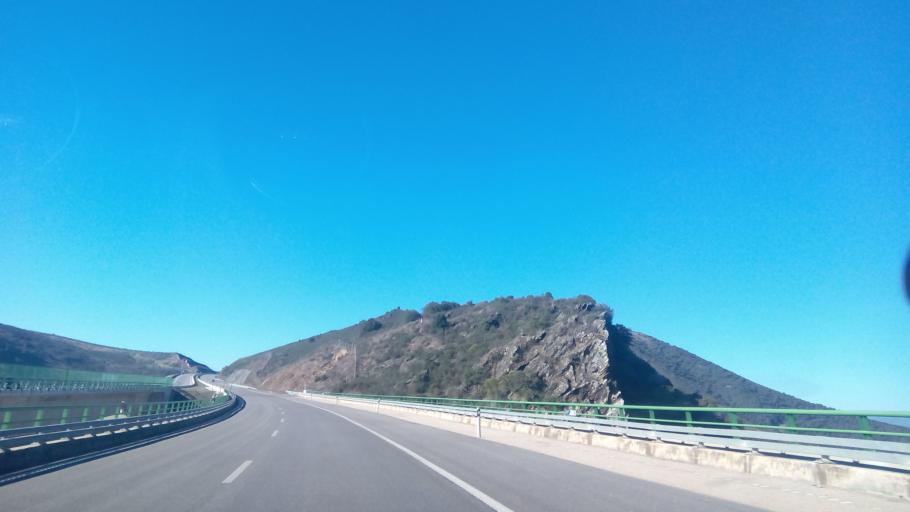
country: PT
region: Braganca
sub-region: Braganca Municipality
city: Braganca
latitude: 41.7766
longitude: -6.6781
